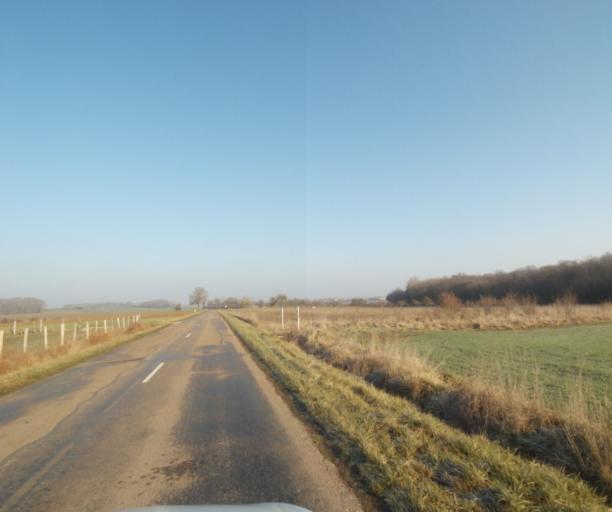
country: FR
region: Champagne-Ardenne
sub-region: Departement de la Haute-Marne
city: Montier-en-Der
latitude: 48.4394
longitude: 4.7563
